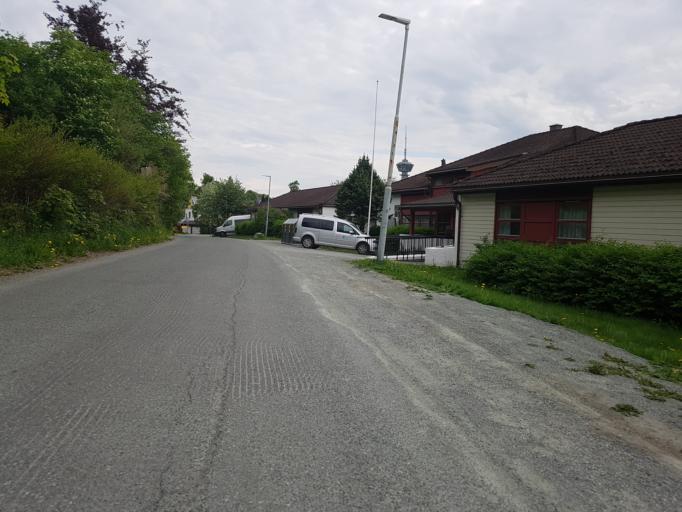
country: NO
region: Sor-Trondelag
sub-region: Trondheim
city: Trondheim
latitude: 63.4286
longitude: 10.4318
